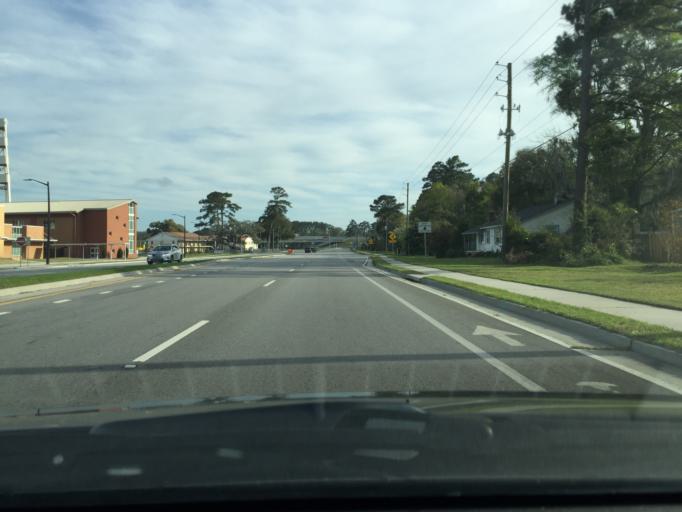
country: US
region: Georgia
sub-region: Chatham County
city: Montgomery
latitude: 31.9779
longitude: -81.1059
